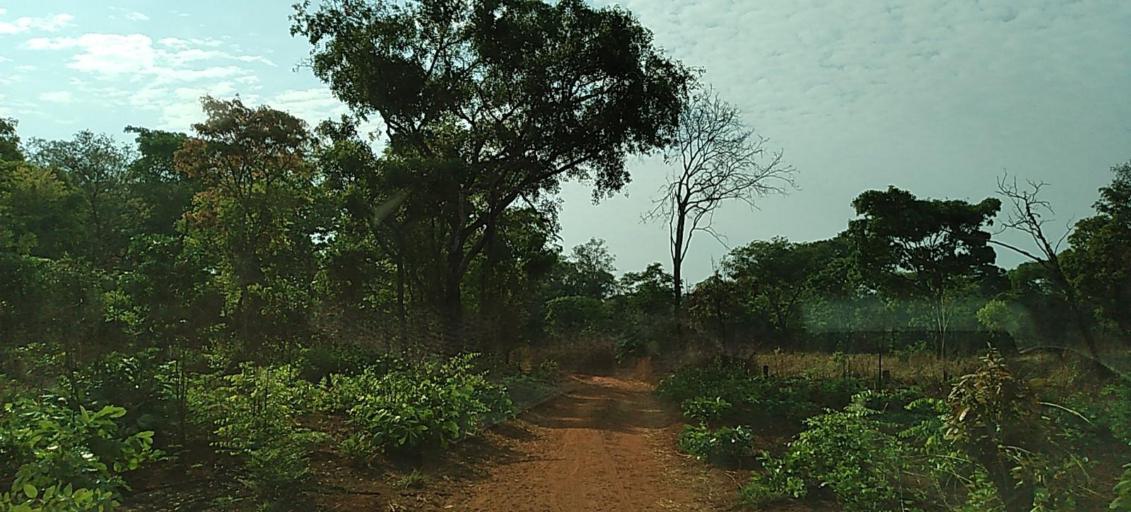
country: ZM
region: Copperbelt
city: Kalulushi
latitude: -12.9632
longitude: 27.7113
